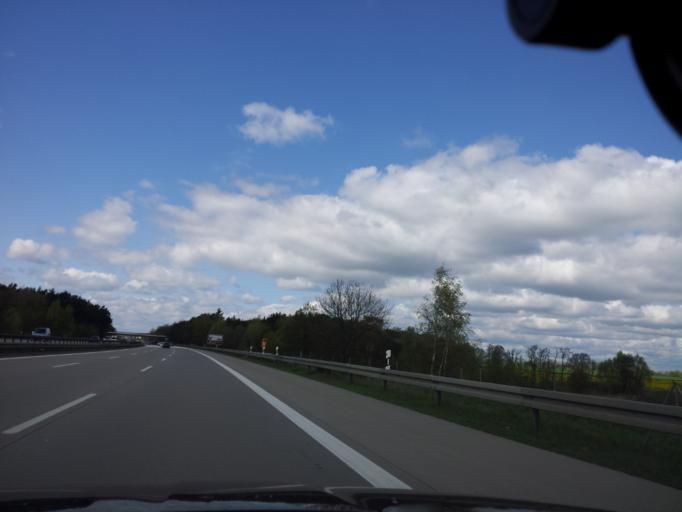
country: DE
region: Berlin
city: Hellersdorf
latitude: 52.5786
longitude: 13.6390
